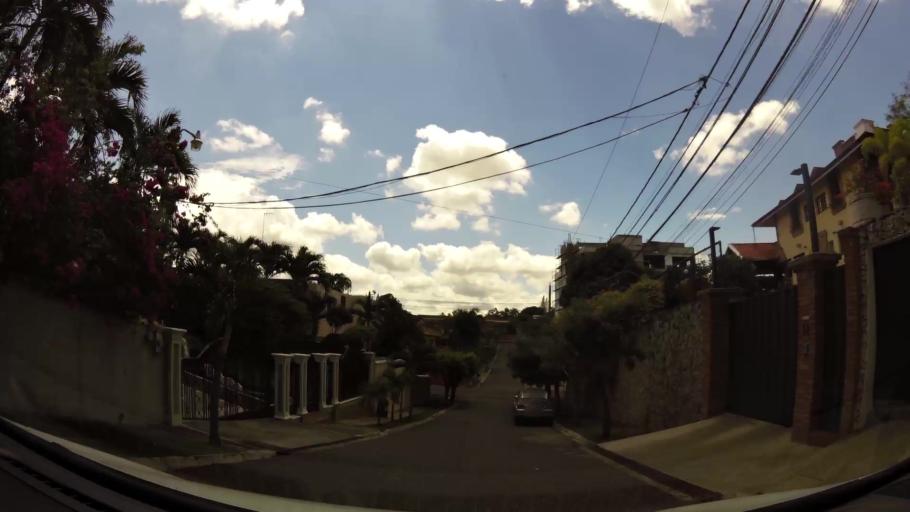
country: DO
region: Santiago
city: Santiago de los Caballeros
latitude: 19.4696
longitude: -70.6769
